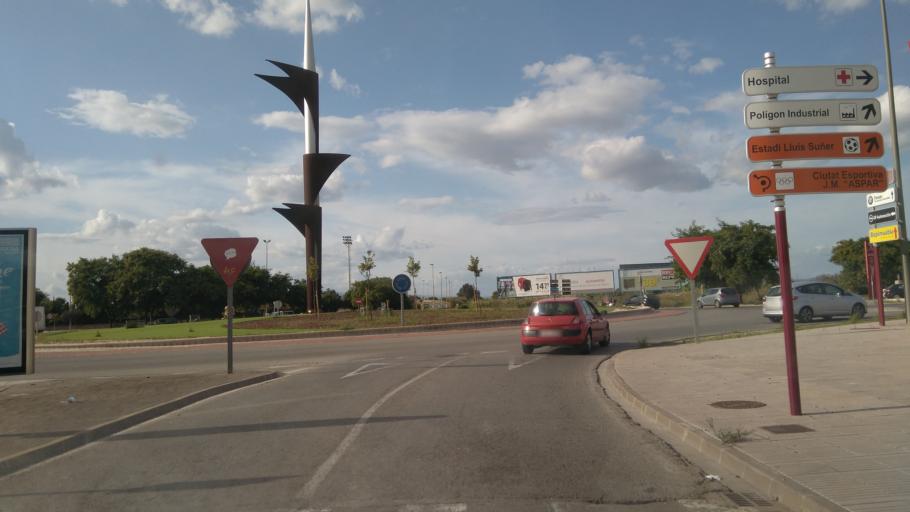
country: ES
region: Valencia
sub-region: Provincia de Valencia
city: Alzira
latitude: 39.1602
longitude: -0.4312
